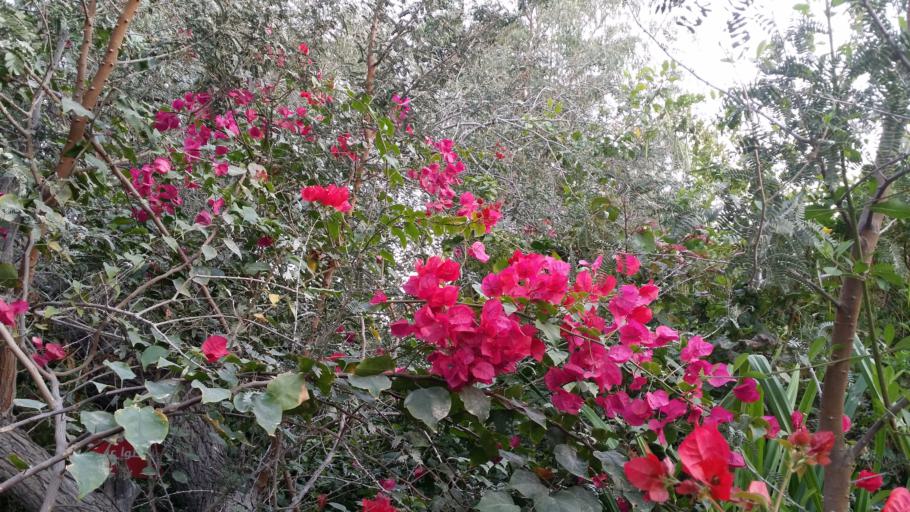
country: AE
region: Ash Shariqah
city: Sharjah
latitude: 25.3348
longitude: 55.3840
